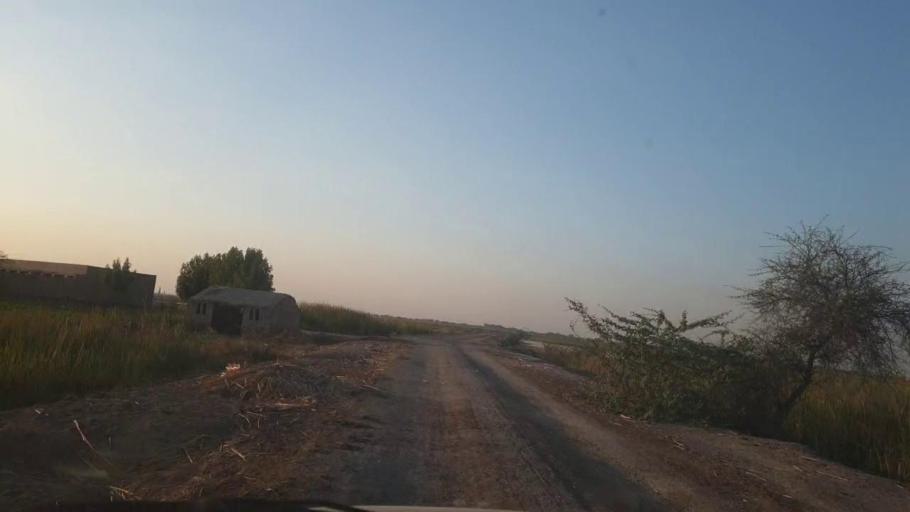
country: PK
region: Sindh
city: Mirpur Khas
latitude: 25.4543
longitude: 69.0743
